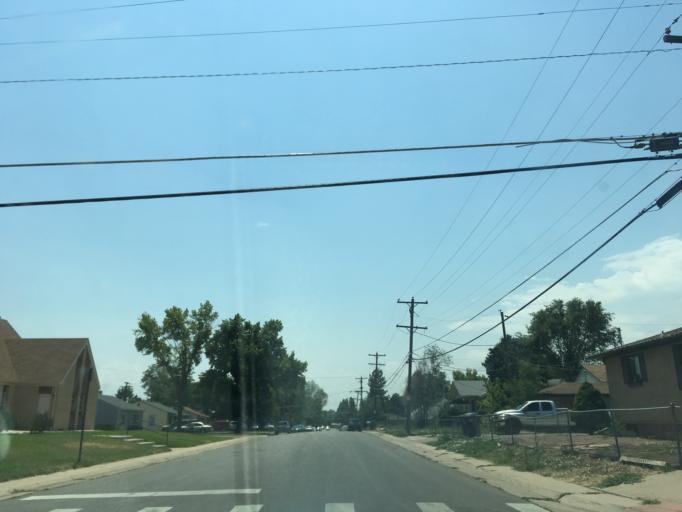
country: US
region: Colorado
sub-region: Arapahoe County
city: Sheridan
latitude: 39.6932
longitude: -105.0321
